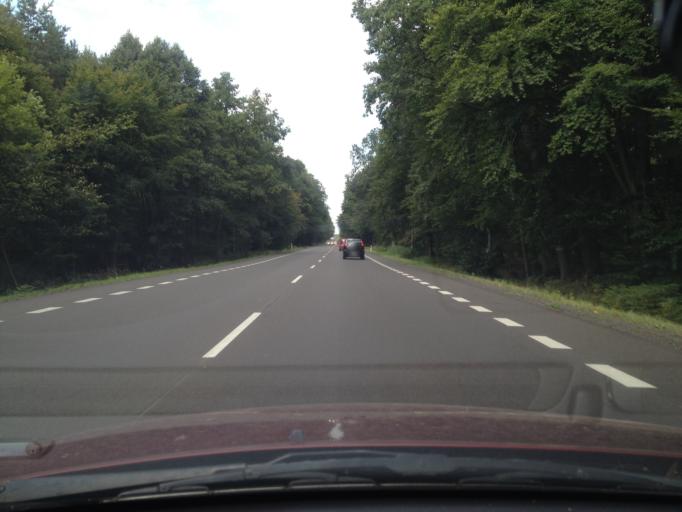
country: PL
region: West Pomeranian Voivodeship
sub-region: Powiat goleniowski
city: Przybiernow
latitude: 53.6680
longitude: 14.8145
